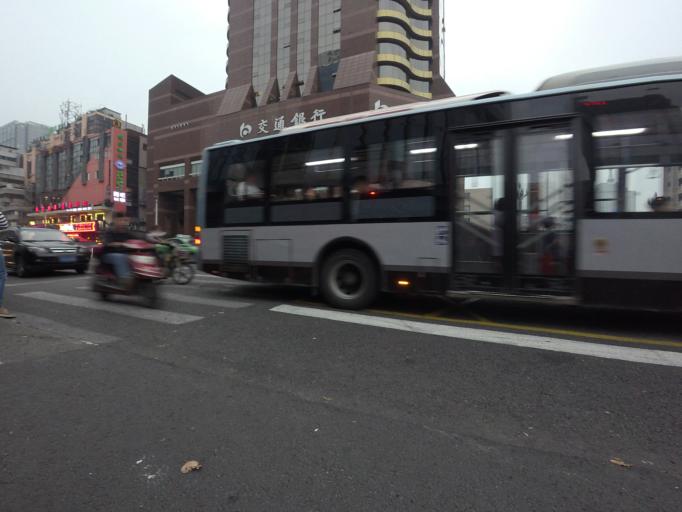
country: CN
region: Sichuan
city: Chengdu
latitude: 30.6697
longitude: 104.0633
